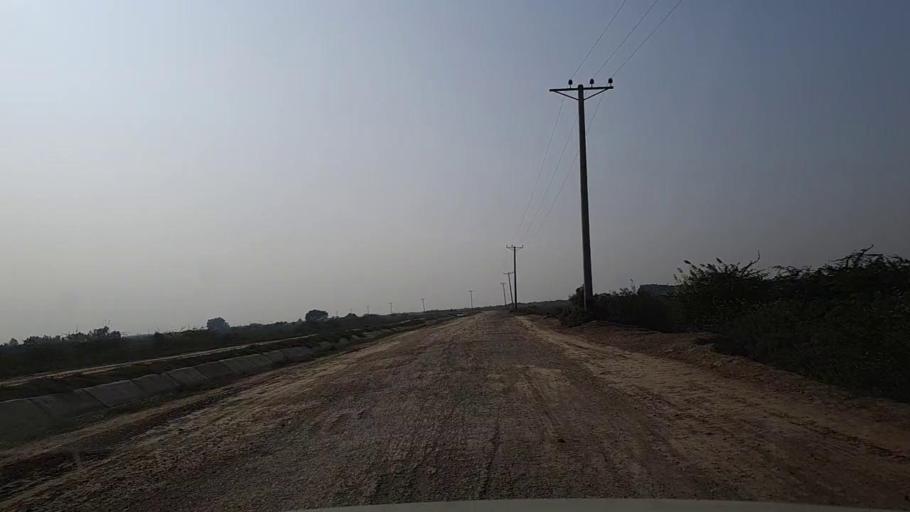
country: PK
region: Sindh
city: Keti Bandar
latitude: 24.2001
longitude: 67.6253
